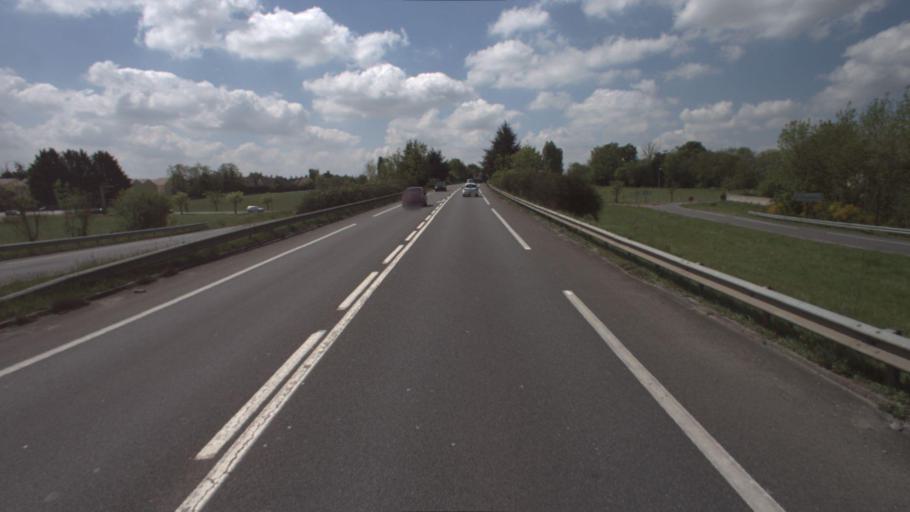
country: FR
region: Ile-de-France
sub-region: Departement de Seine-et-Marne
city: Guignes
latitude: 48.6397
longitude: 2.7934
